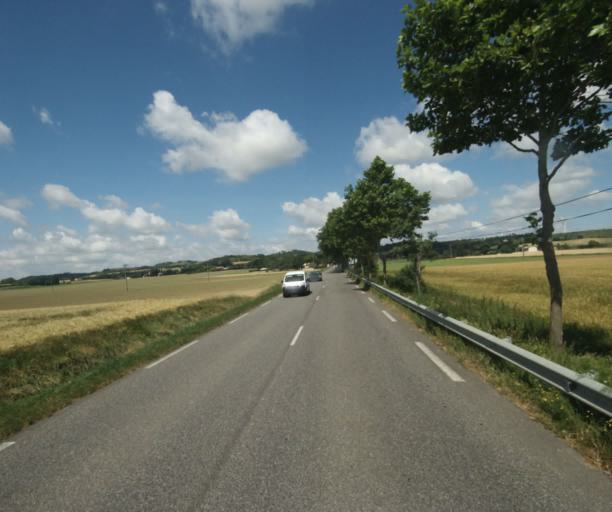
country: FR
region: Midi-Pyrenees
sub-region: Departement de la Haute-Garonne
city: Saint-Felix-Lauragais
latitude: 43.4483
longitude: 1.9224
